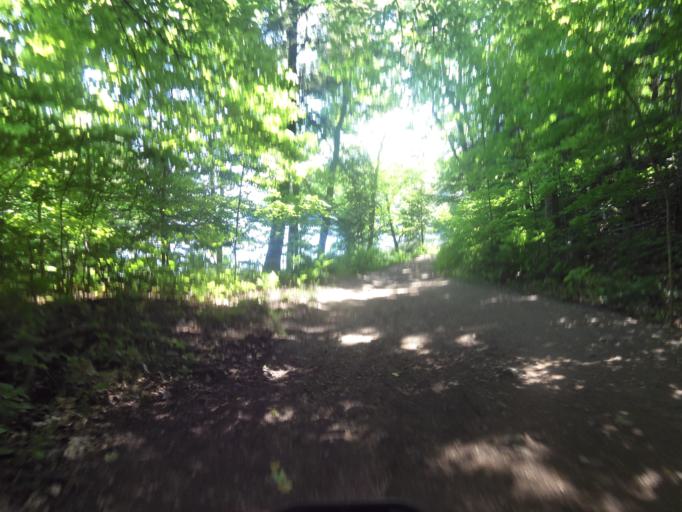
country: CA
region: Quebec
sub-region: Outaouais
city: Wakefield
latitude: 45.5347
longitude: -75.8689
